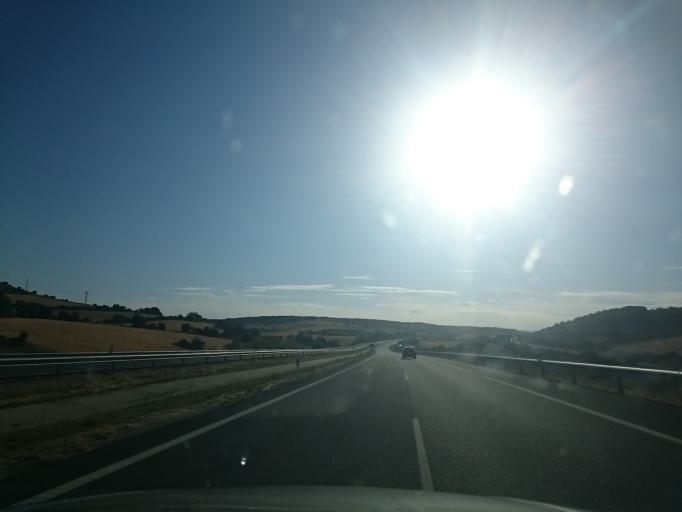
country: ES
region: Castille and Leon
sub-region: Provincia de Burgos
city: Villanueva de Argano
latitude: 42.3802
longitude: -3.9444
